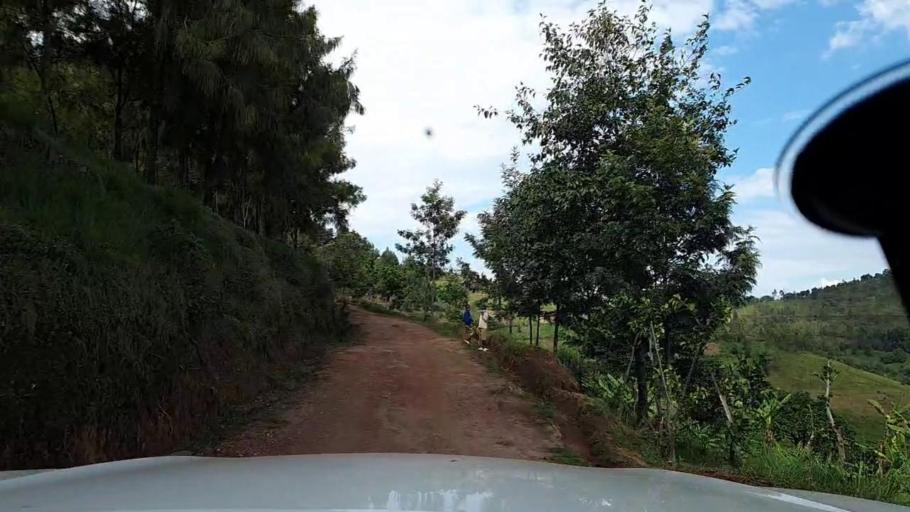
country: RW
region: Kigali
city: Kigali
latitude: -1.7871
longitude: 29.8315
